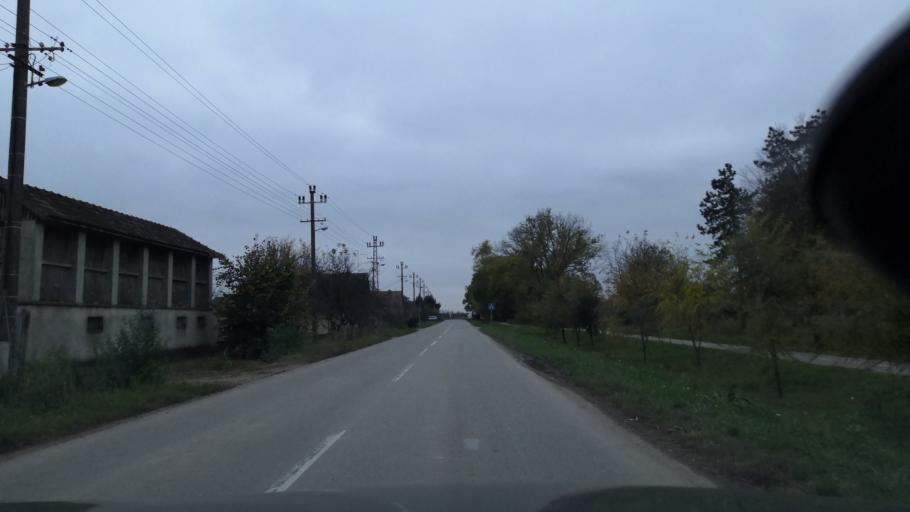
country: HU
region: Csongrad
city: Roszke
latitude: 46.1521
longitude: 20.1059
